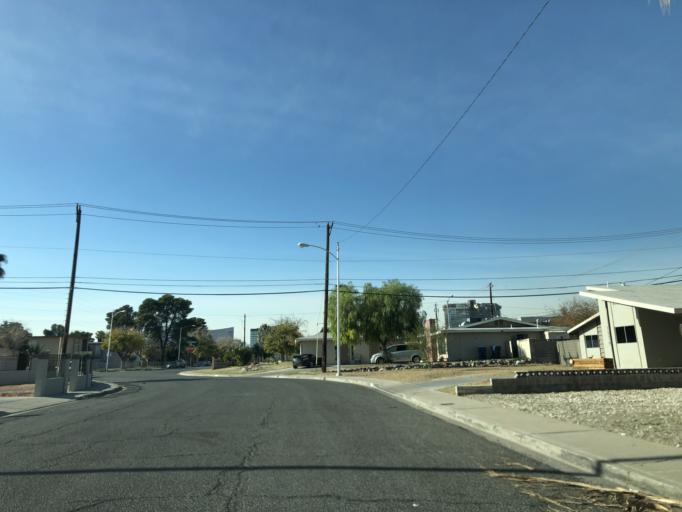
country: US
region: Nevada
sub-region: Clark County
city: Winchester
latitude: 36.1309
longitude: -115.1311
